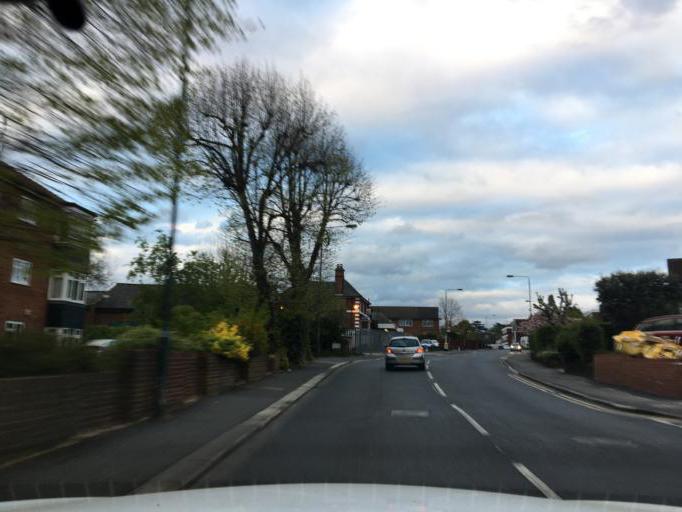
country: GB
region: England
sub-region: Greater London
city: Sidcup
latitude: 51.4281
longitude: 0.0921
